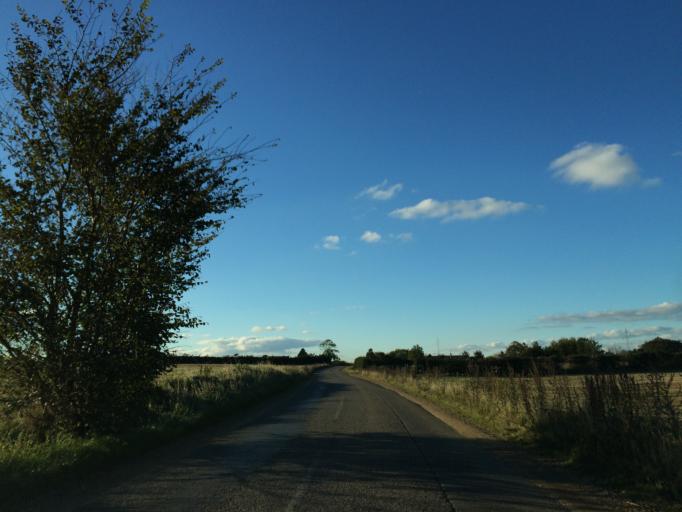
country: DK
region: Central Jutland
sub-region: Skanderborg Kommune
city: Ry
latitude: 56.1411
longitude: 9.7123
